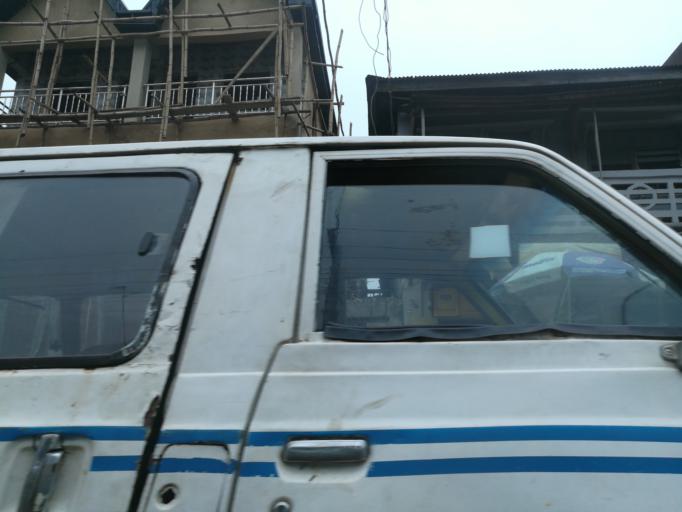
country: NG
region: Lagos
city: Ebute Metta
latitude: 6.4824
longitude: 3.3873
